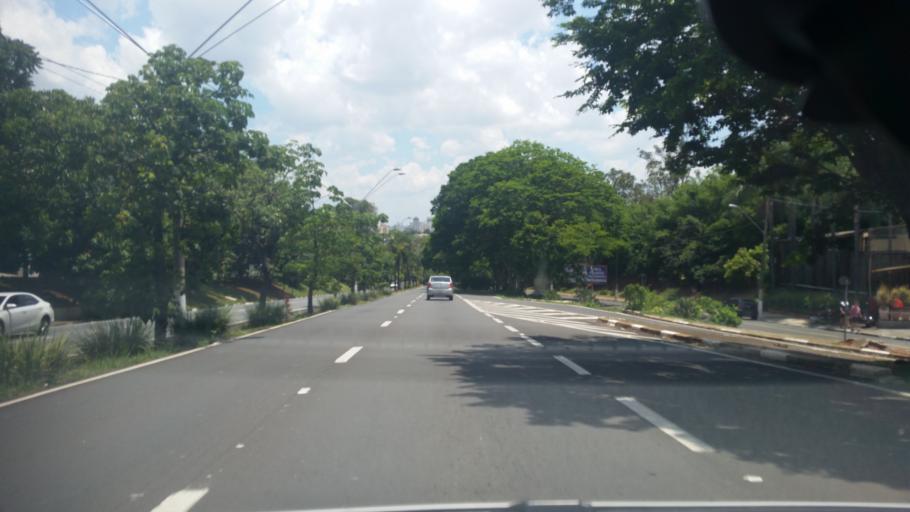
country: BR
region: Sao Paulo
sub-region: Campinas
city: Campinas
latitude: -22.8690
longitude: -47.0446
